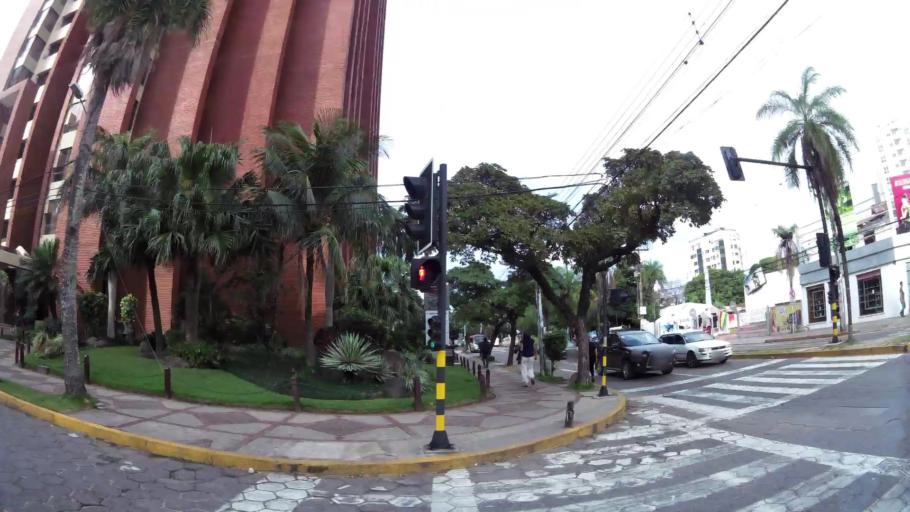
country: BO
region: Santa Cruz
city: Santa Cruz de la Sierra
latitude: -17.7916
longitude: -63.1766
